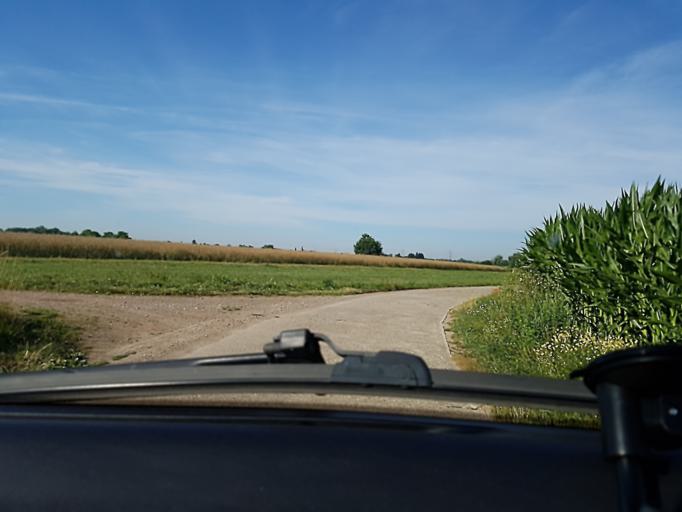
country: DE
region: Baden-Wuerttemberg
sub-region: Freiburg Region
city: Willstatt
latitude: 48.5816
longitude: 7.8804
